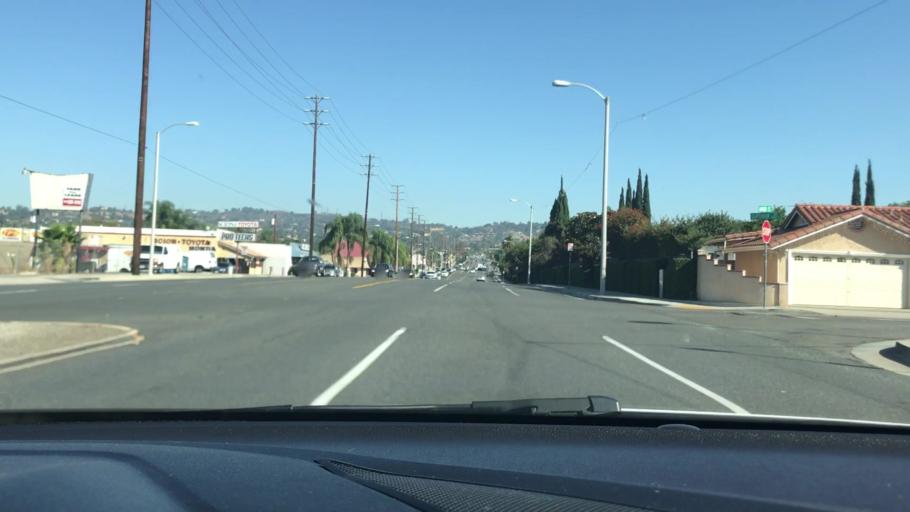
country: US
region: California
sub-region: Orange County
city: La Habra
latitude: 33.9279
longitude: -117.9330
